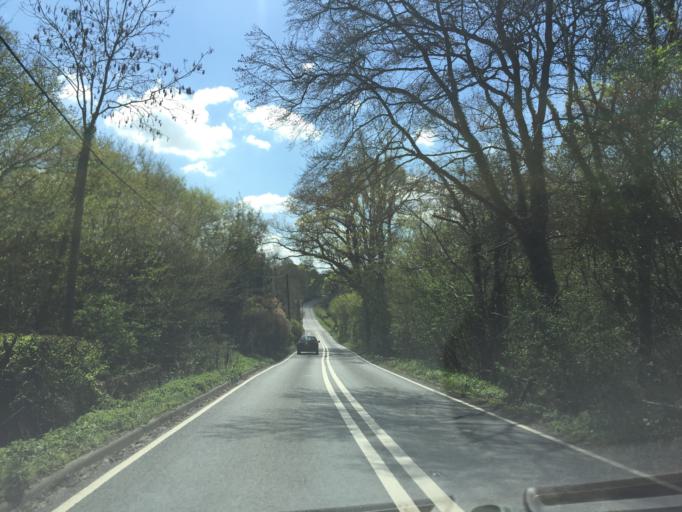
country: GB
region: England
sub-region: Kent
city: Edenbridge
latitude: 51.1457
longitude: 0.1062
